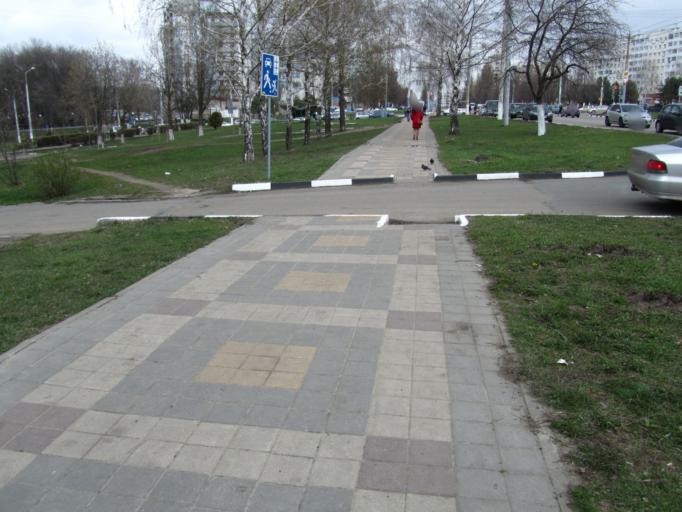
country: RU
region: Belgorod
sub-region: Belgorodskiy Rayon
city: Belgorod
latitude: 50.5789
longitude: 36.5811
